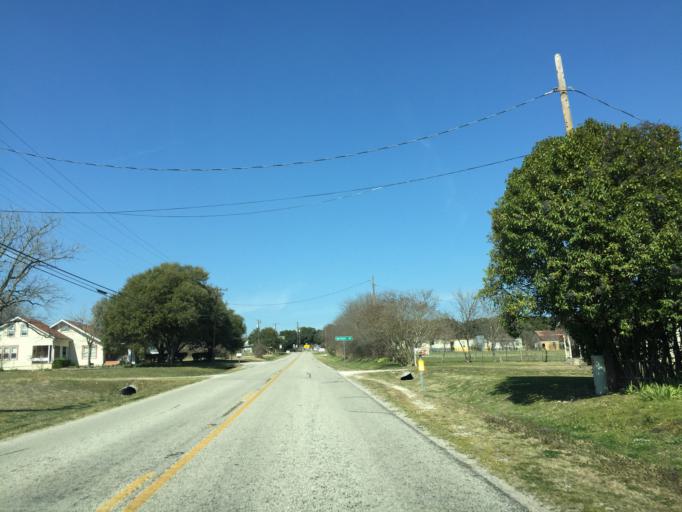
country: US
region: Texas
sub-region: Williamson County
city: Serenada
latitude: 30.7328
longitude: -97.5865
